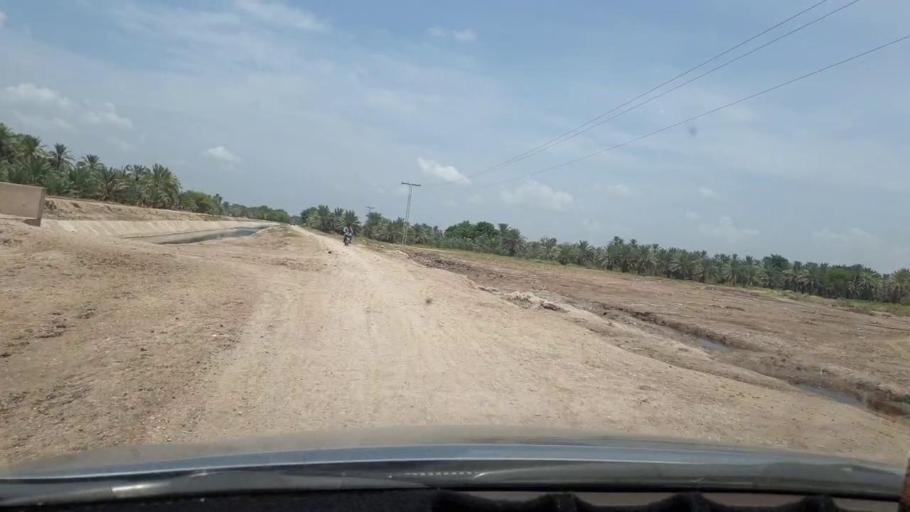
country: PK
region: Sindh
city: Khairpur
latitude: 27.4360
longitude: 68.7819
